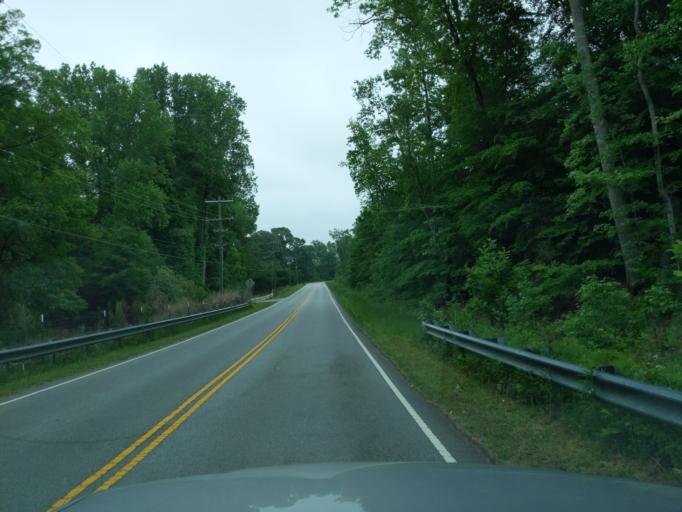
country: US
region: South Carolina
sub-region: Greenville County
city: Five Forks
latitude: 34.8566
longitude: -82.2067
